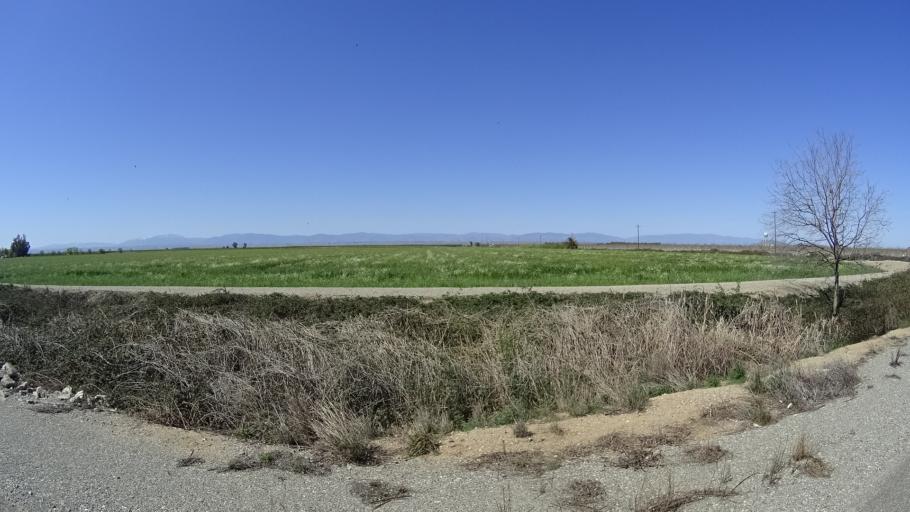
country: US
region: California
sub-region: Glenn County
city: Orland
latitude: 39.6751
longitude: -122.2340
